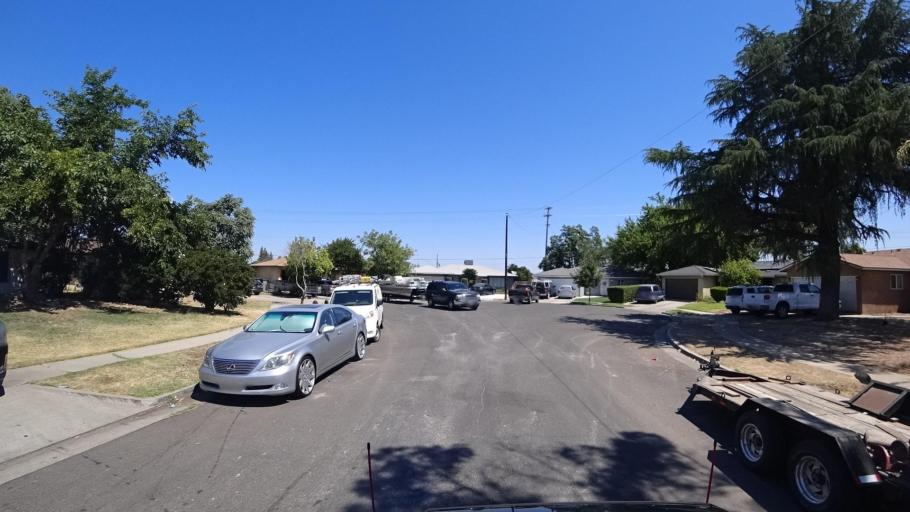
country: US
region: California
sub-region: Fresno County
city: Fresno
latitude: 36.7640
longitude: -119.7505
